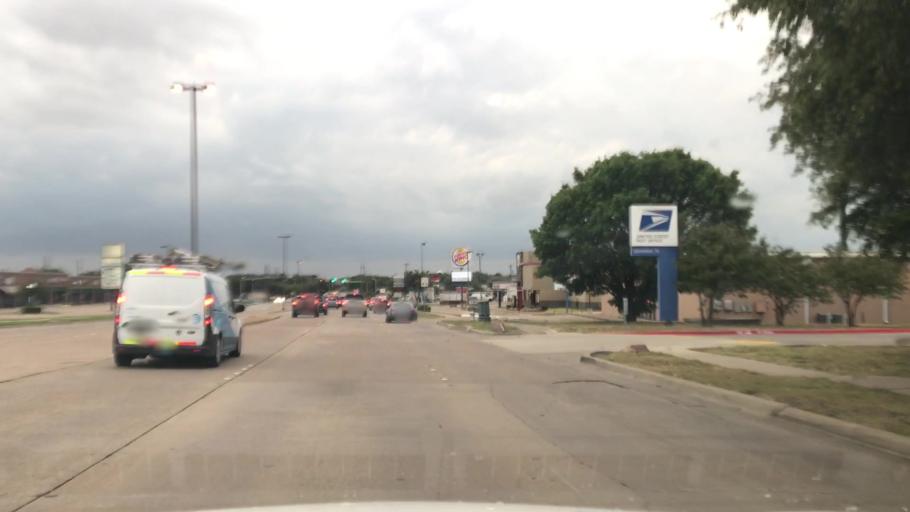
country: US
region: Texas
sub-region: Dallas County
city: Carrollton
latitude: 33.0139
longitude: -96.8871
